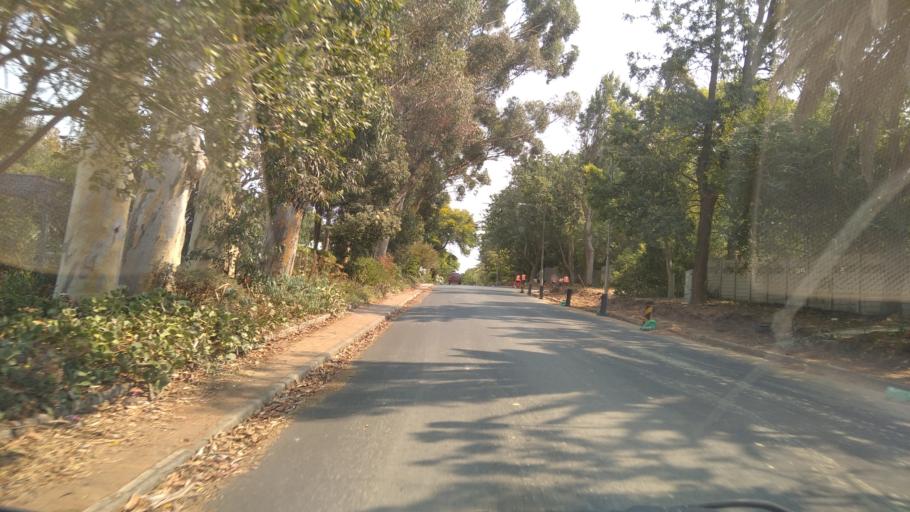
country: ZA
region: Western Cape
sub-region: City of Cape Town
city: Kraaifontein
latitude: -33.8189
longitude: 18.6578
